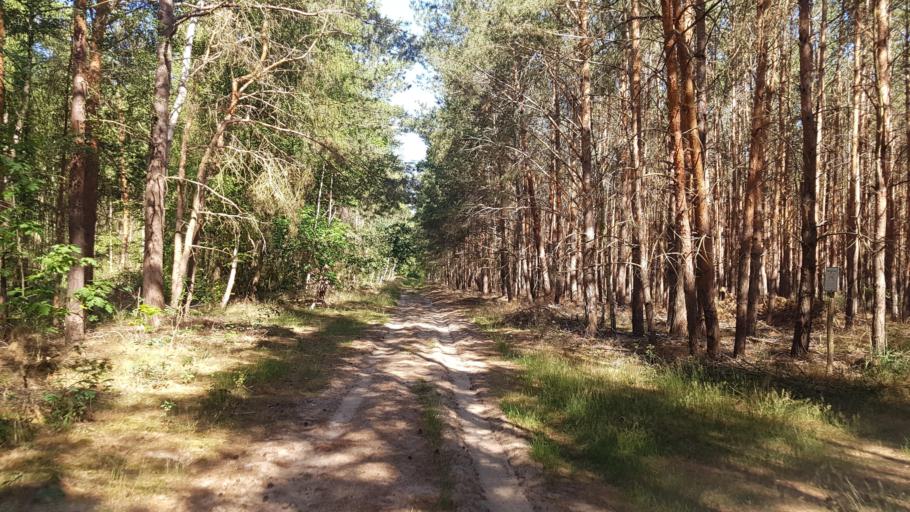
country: DE
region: Brandenburg
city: Juterbog
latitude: 51.9759
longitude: 13.1442
